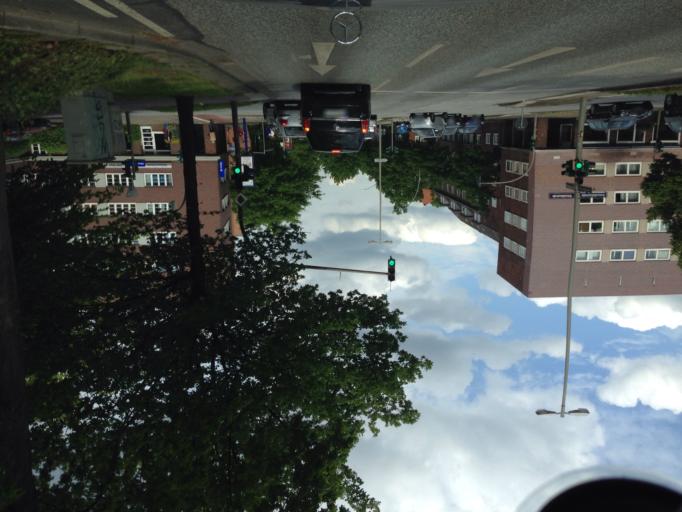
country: DE
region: Hamburg
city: Marienthal
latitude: 53.5846
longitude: 10.0779
